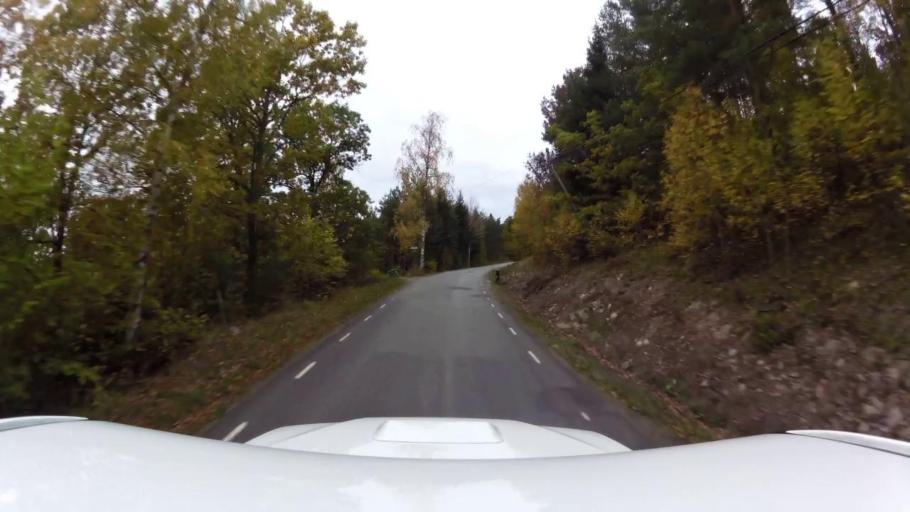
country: SE
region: OEstergoetland
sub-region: Linkopings Kommun
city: Ljungsbro
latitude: 58.5411
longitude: 15.4148
